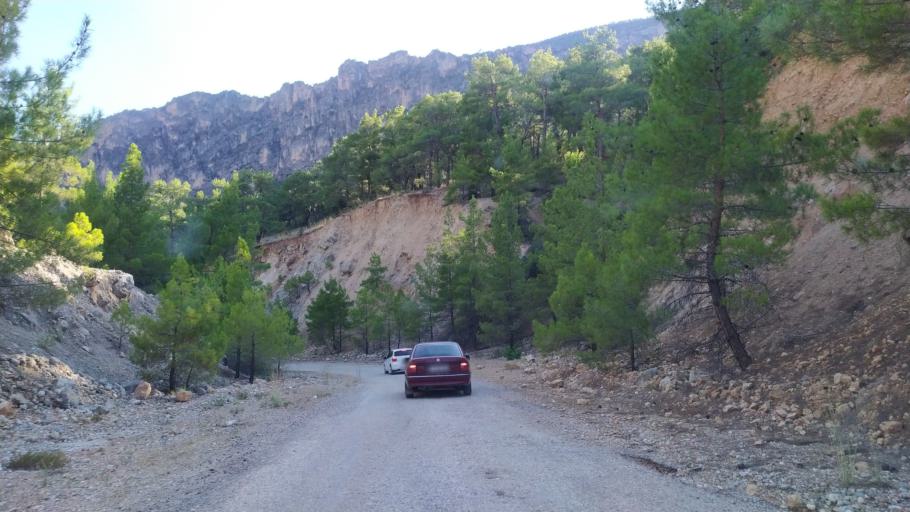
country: TR
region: Mersin
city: Mut
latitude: 36.5467
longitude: 33.2339
